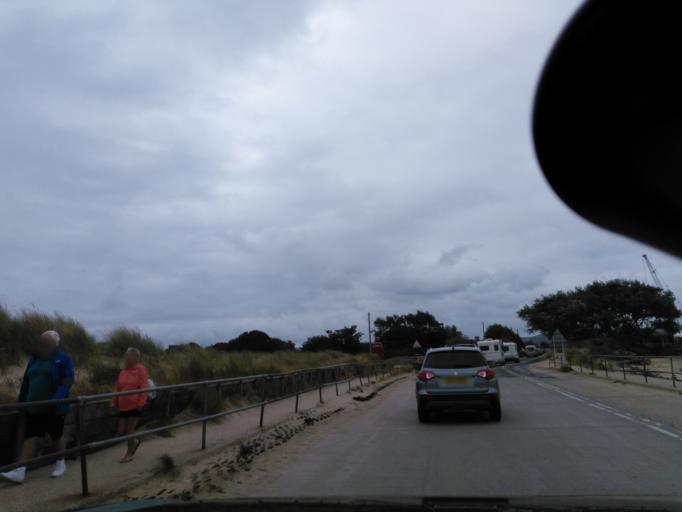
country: GB
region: England
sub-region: Dorset
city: Parkstone
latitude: 50.6793
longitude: -1.9503
